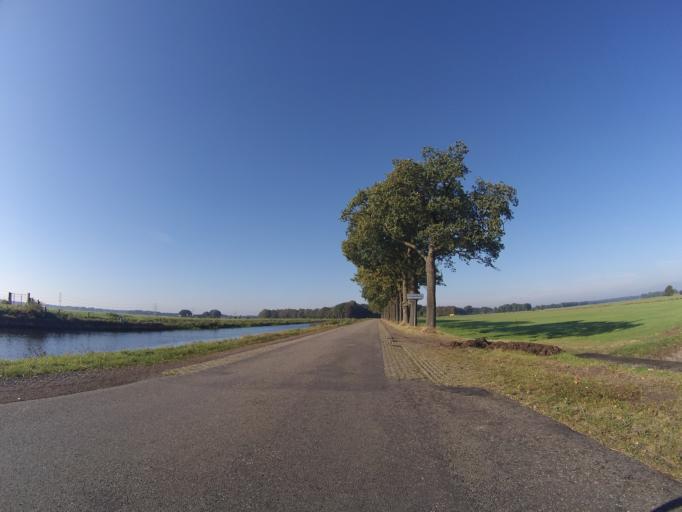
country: NL
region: Drenthe
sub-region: Gemeente Coevorden
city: Sleen
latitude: 52.7387
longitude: 6.7790
